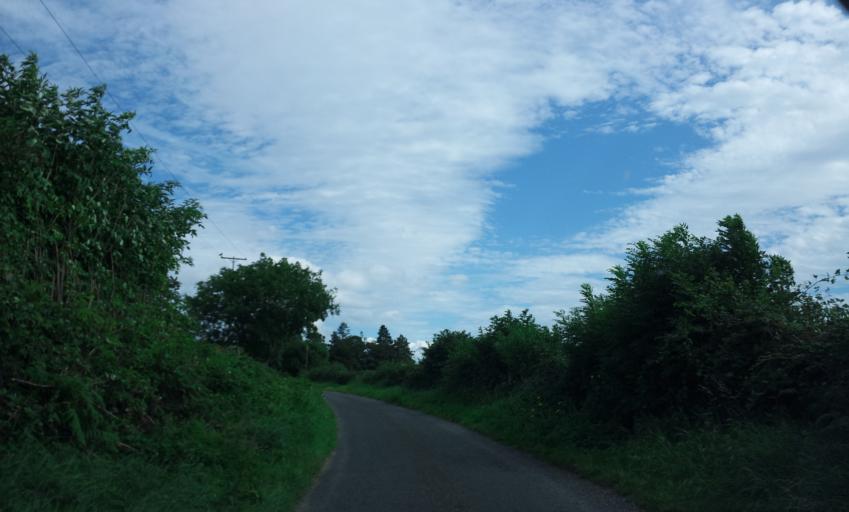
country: IE
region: Leinster
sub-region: Laois
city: Stradbally
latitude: 53.0128
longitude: -7.1994
